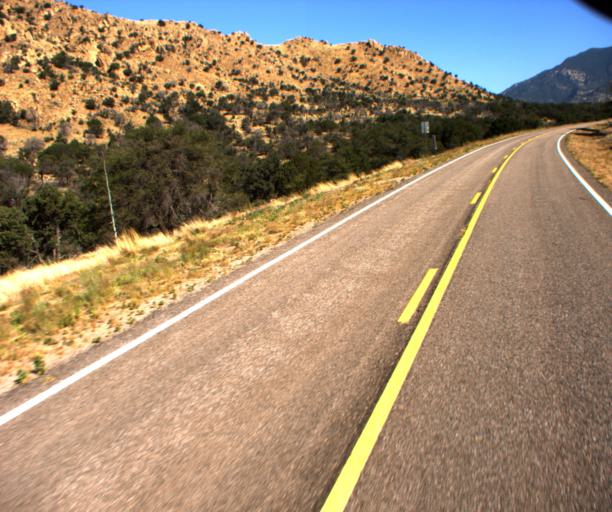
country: US
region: Arizona
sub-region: Graham County
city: Swift Trail Junction
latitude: 32.5843
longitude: -109.8534
